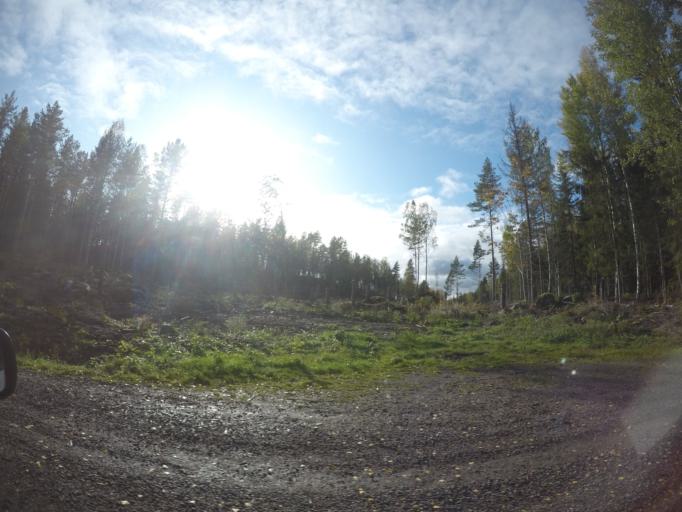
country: SE
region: Soedermanland
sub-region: Eskilstuna Kommun
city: Kvicksund
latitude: 59.3619
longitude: 16.2635
